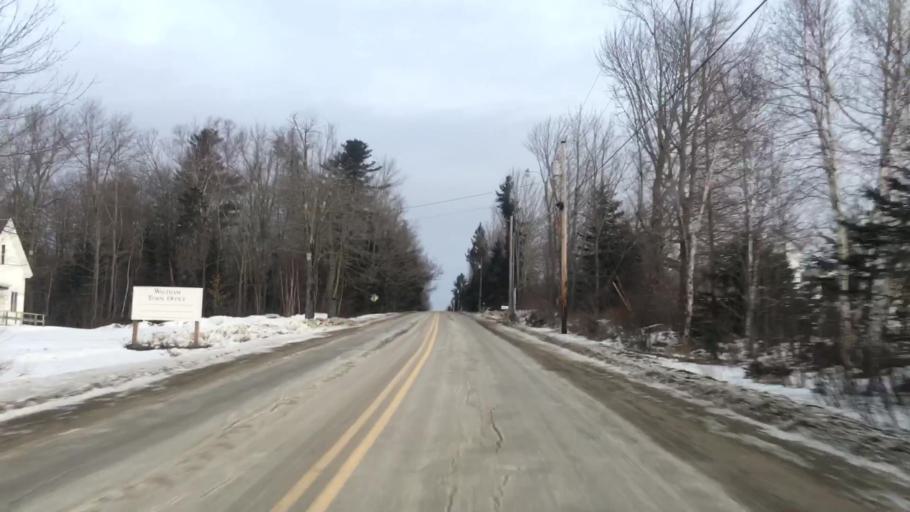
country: US
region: Maine
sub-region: Hancock County
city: Franklin
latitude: 44.7243
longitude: -68.3344
